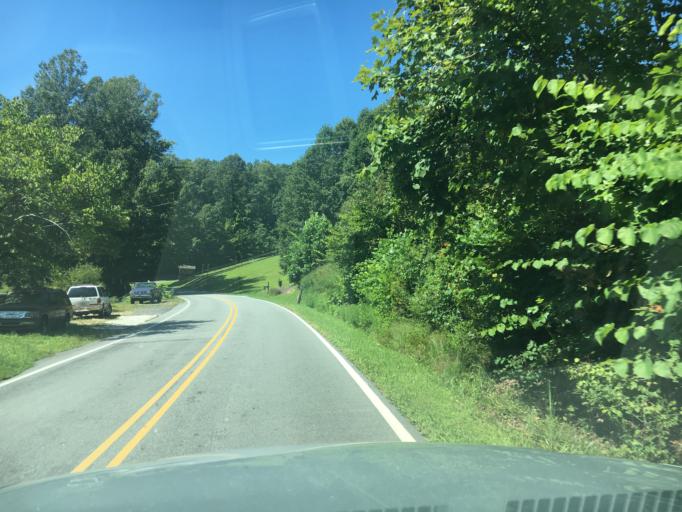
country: US
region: North Carolina
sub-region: McDowell County
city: West Marion
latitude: 35.6681
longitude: -82.0336
